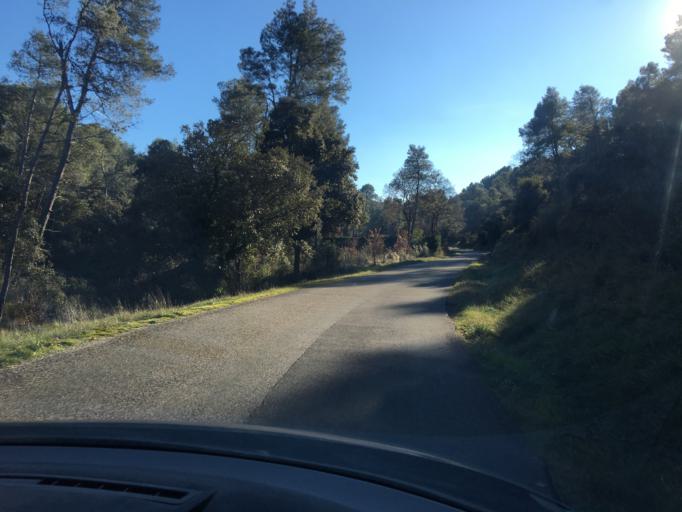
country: FR
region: Provence-Alpes-Cote d'Azur
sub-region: Departement des Bouches-du-Rhone
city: Saint-Remy-de-Provence
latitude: 43.7671
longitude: 4.7941
